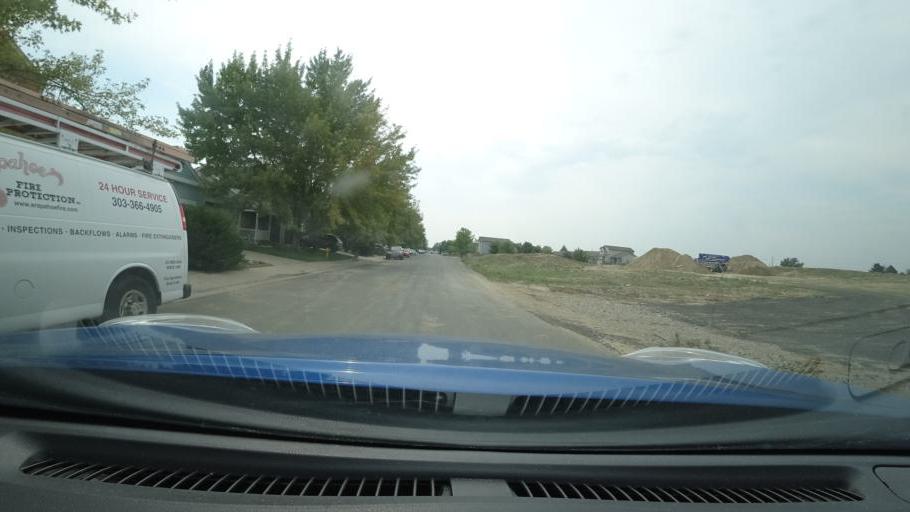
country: US
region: Colorado
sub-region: Adams County
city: Aurora
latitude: 39.7504
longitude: -104.7638
